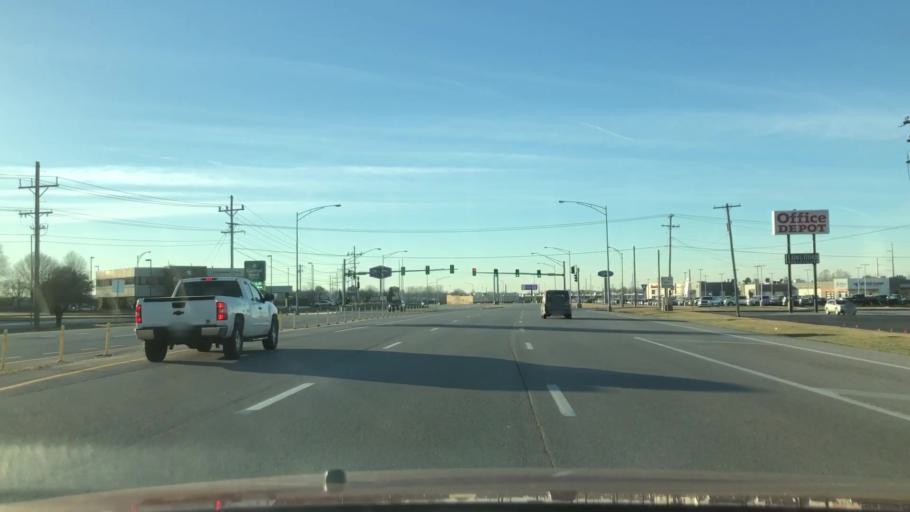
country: US
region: Missouri
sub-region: Greene County
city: Springfield
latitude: 37.1575
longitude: -93.2629
